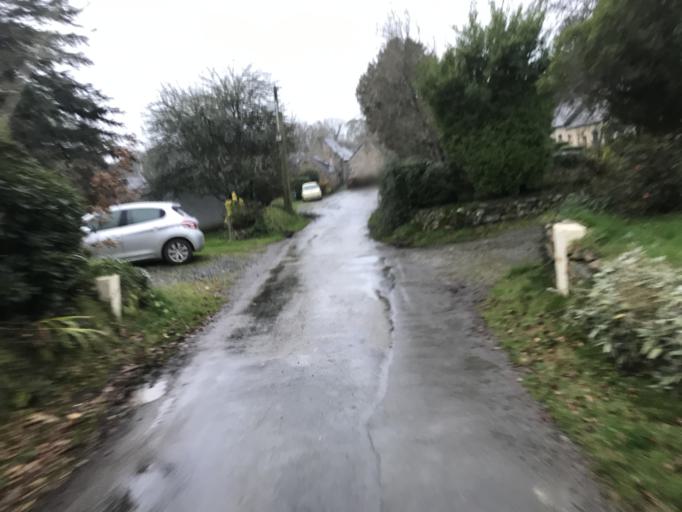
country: FR
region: Brittany
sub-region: Departement du Finistere
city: Logonna-Daoulas
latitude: 48.3222
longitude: -4.2787
